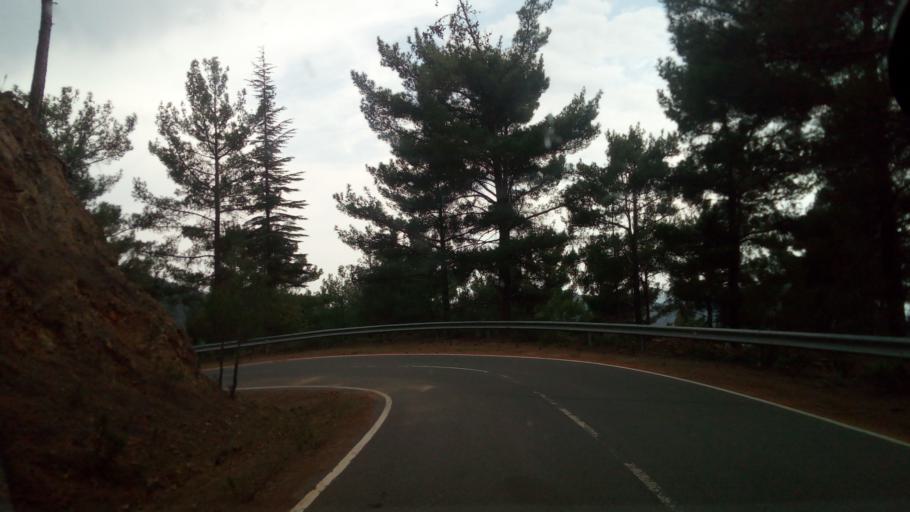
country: CY
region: Lefkosia
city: Kato Pyrgos
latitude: 35.0110
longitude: 32.6633
